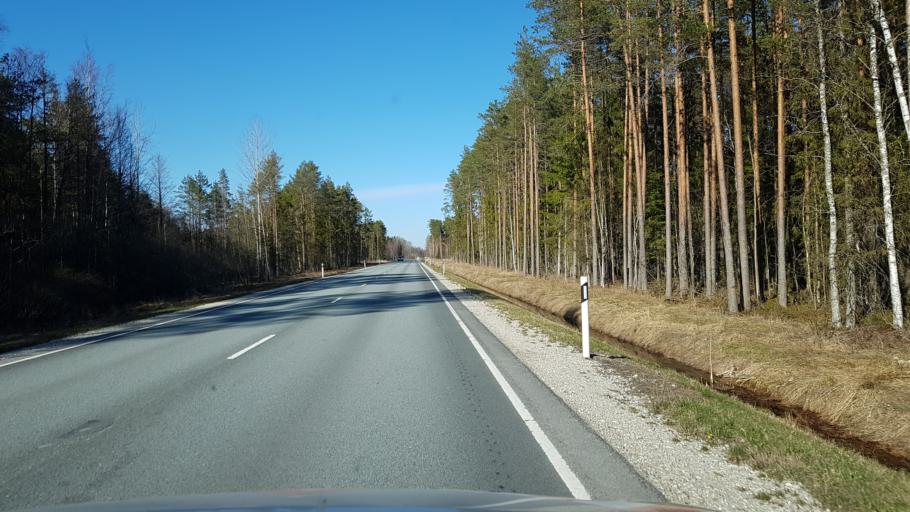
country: EE
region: Jogevamaa
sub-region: Mustvee linn
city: Mustvee
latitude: 58.8733
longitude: 26.9446
